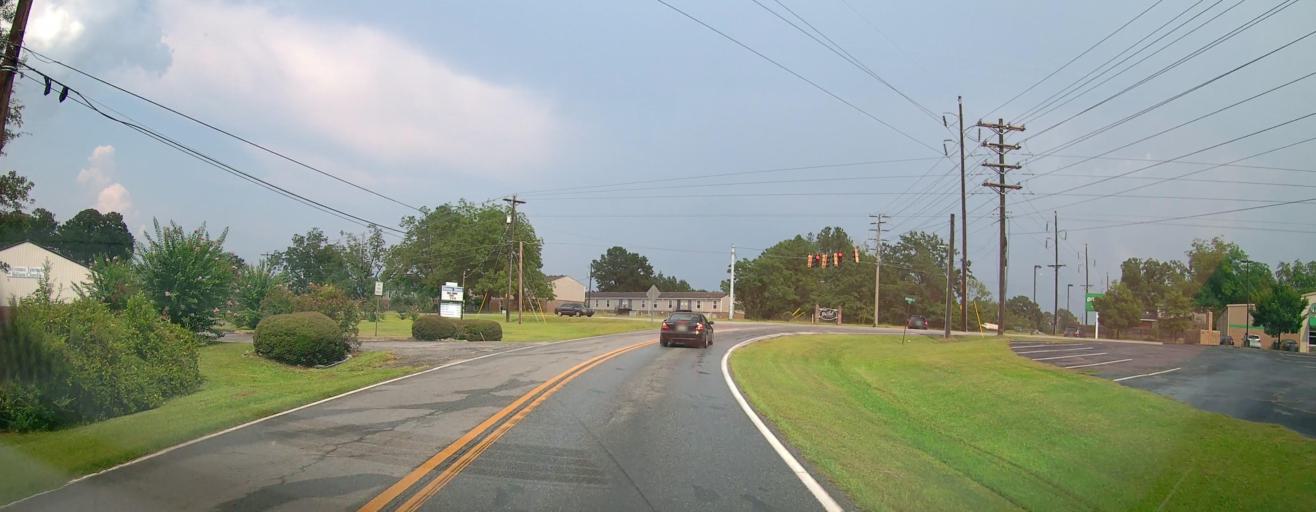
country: US
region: Georgia
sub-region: Houston County
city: Warner Robins
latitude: 32.6510
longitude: -83.6268
